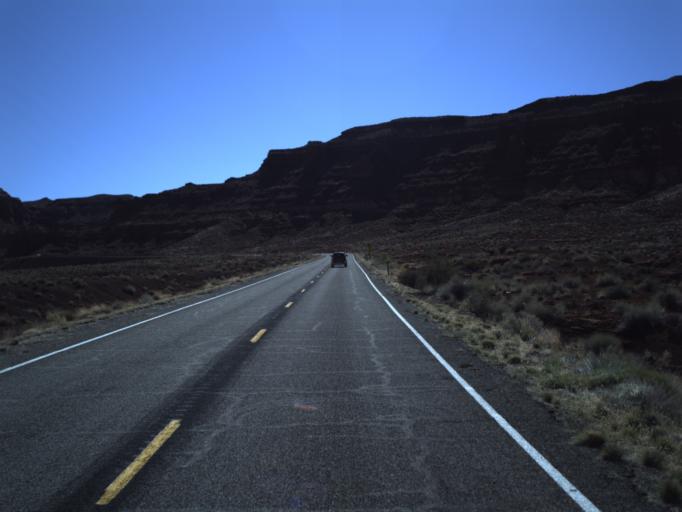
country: US
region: Utah
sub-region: San Juan County
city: Blanding
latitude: 37.8757
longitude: -110.3493
